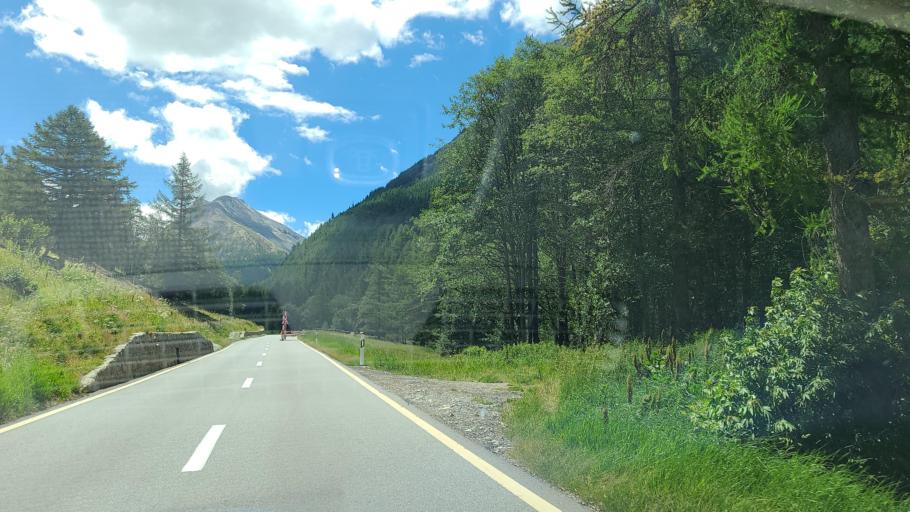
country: CH
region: Valais
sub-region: Visp District
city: Saas-Grund
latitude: 46.1087
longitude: 7.9442
